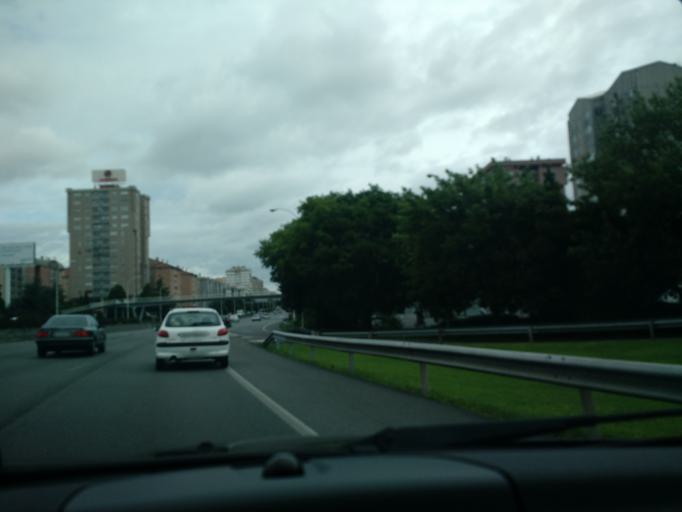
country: ES
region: Galicia
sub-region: Provincia da Coruna
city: A Coruna
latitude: 43.3438
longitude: -8.4087
